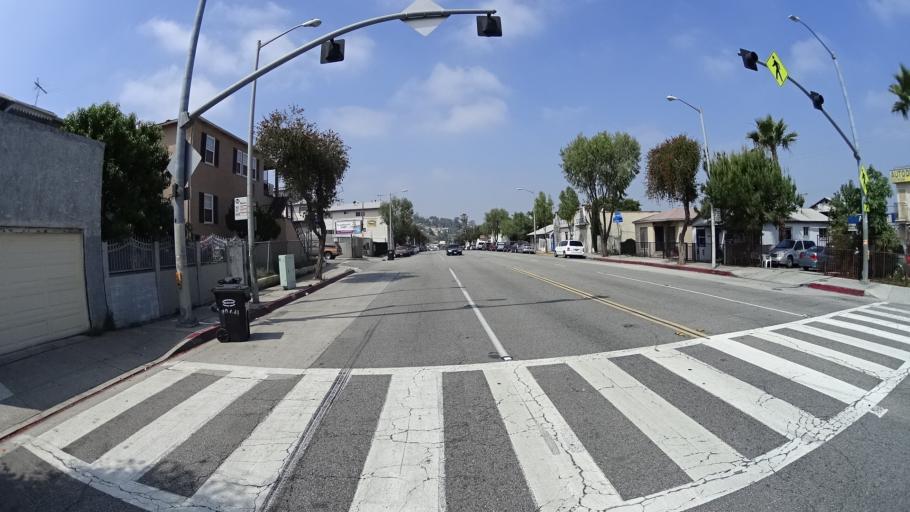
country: US
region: California
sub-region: Los Angeles County
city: Belvedere
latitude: 34.0572
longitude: -118.1737
